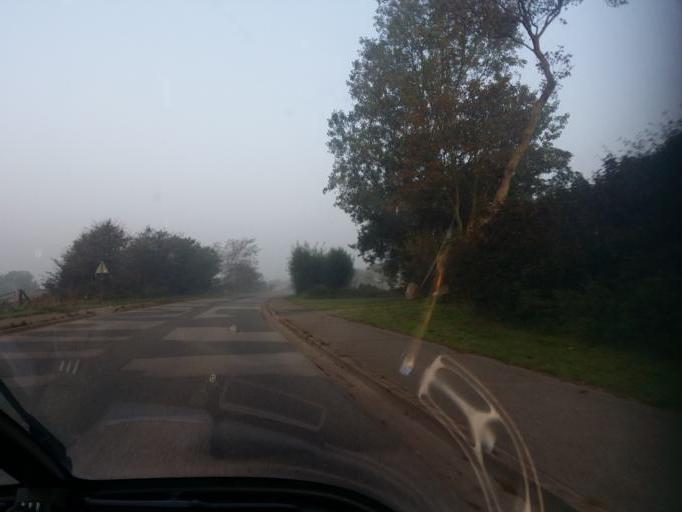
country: DE
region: Schleswig-Holstein
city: Schobull
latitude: 54.5018
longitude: 9.0148
